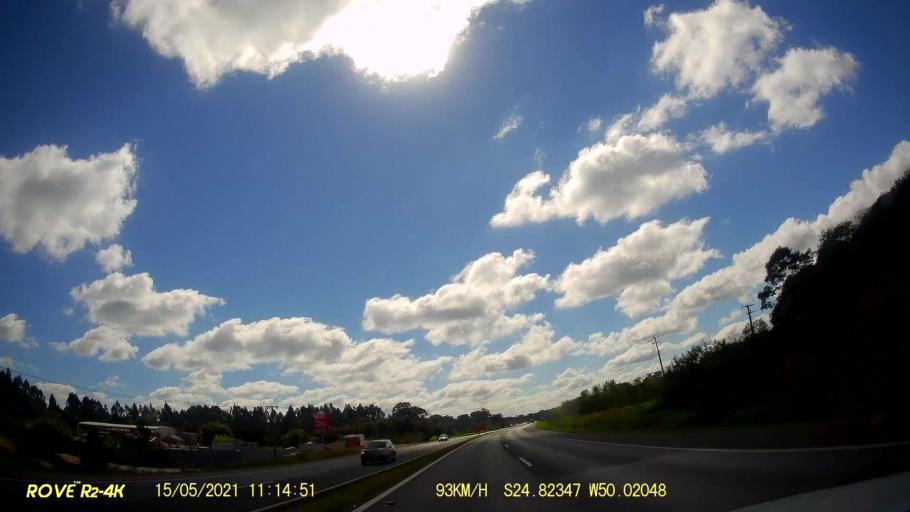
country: BR
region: Parana
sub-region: Castro
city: Castro
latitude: -24.8236
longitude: -50.0205
